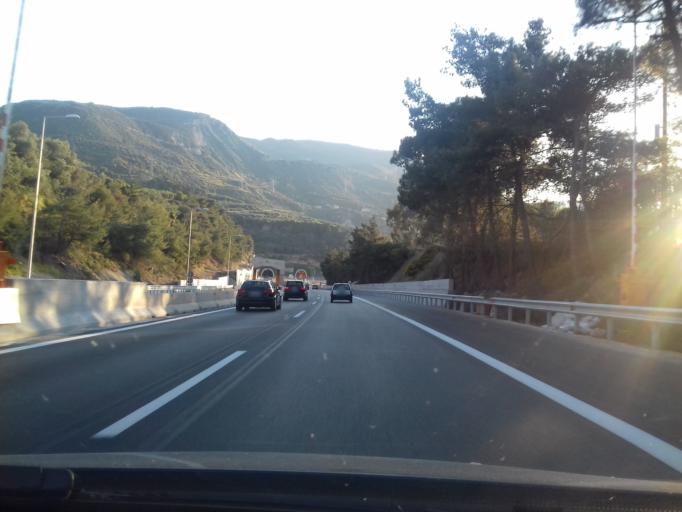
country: GR
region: West Greece
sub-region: Nomos Achaias
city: Akrata
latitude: 38.1701
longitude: 22.2847
